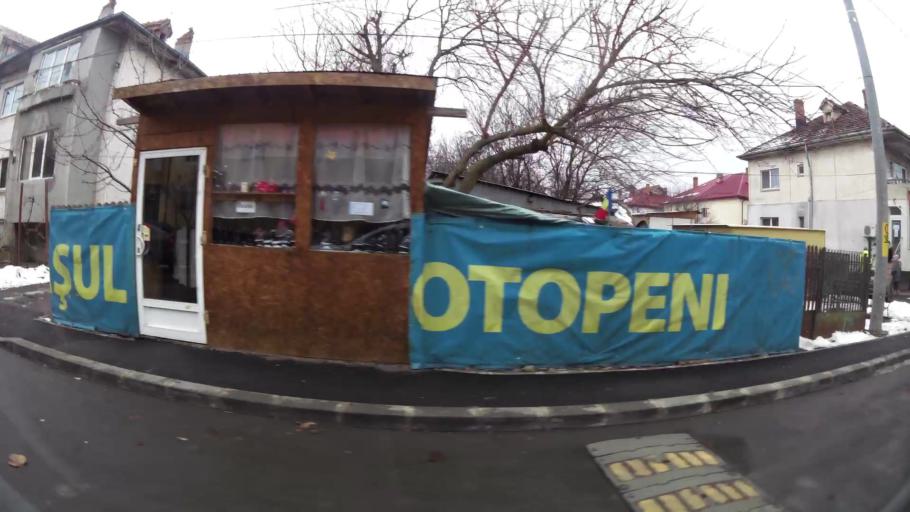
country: RO
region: Ilfov
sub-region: Comuna Otopeni
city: Otopeni
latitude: 44.5531
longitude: 26.0721
